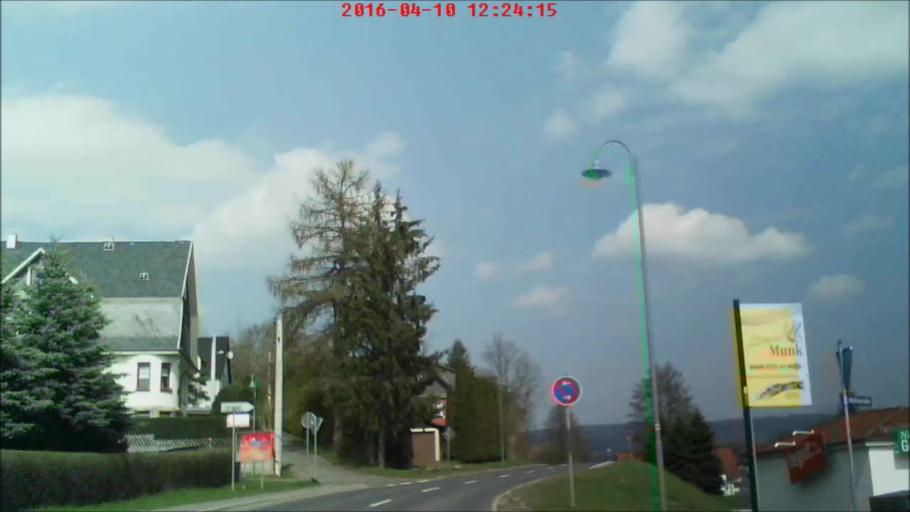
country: DE
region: Thuringia
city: Viernau
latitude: 50.6691
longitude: 10.5519
